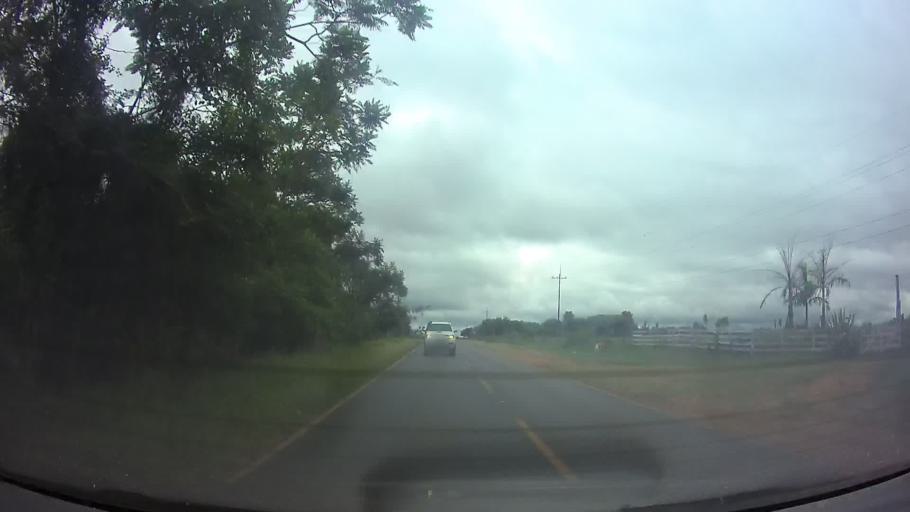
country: PY
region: Central
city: Guarambare
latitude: -25.5206
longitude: -57.4925
